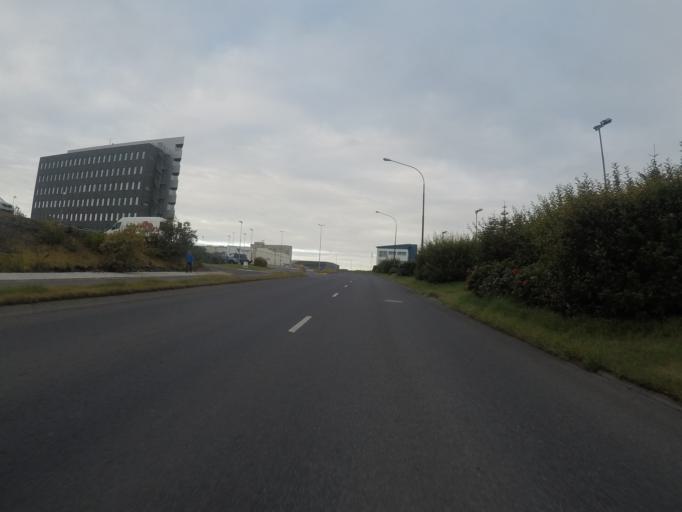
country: IS
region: Capital Region
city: Reykjavik
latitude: 64.1511
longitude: -21.8678
